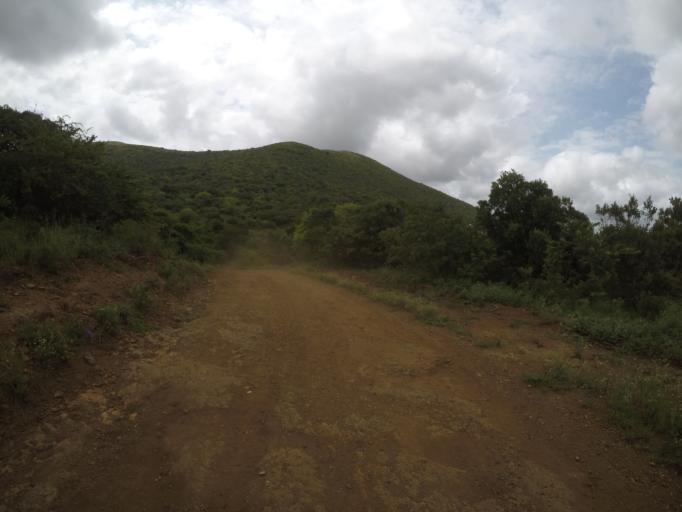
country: ZA
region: KwaZulu-Natal
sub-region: uThungulu District Municipality
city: Empangeni
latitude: -28.5868
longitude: 31.8698
